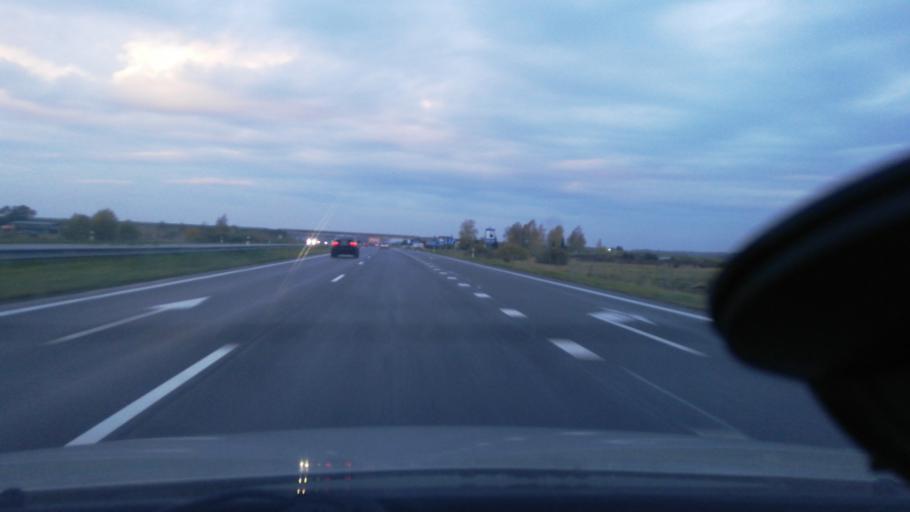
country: LT
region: Klaipedos apskritis
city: Gargzdai
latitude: 55.7324
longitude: 21.3892
